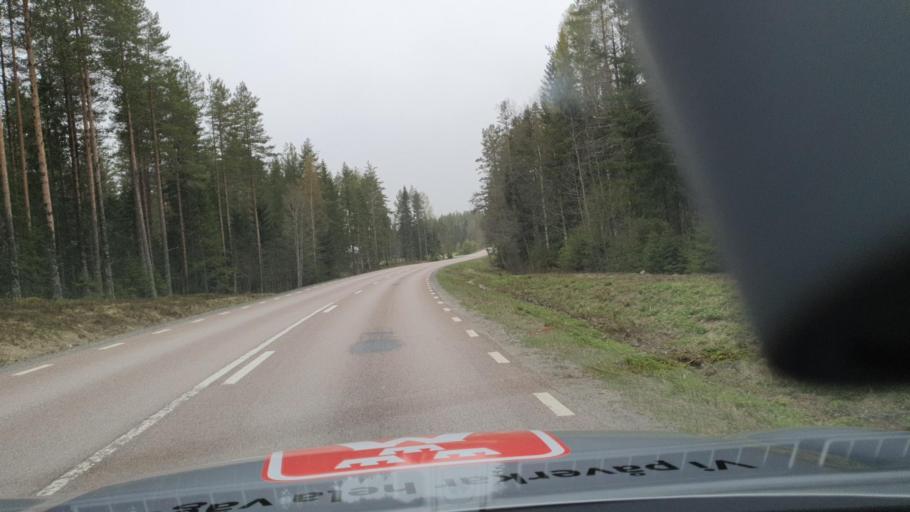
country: SE
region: Vaesternorrland
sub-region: OErnskoeldsviks Kommun
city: Ornskoldsvik
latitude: 63.3658
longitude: 18.8706
